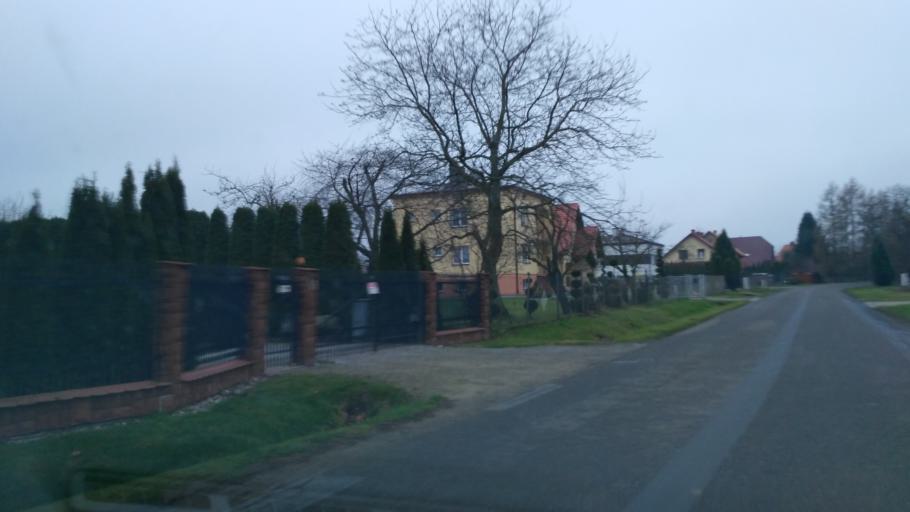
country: PL
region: Subcarpathian Voivodeship
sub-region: Powiat przeworski
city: Rozborz
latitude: 50.0611
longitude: 22.5223
